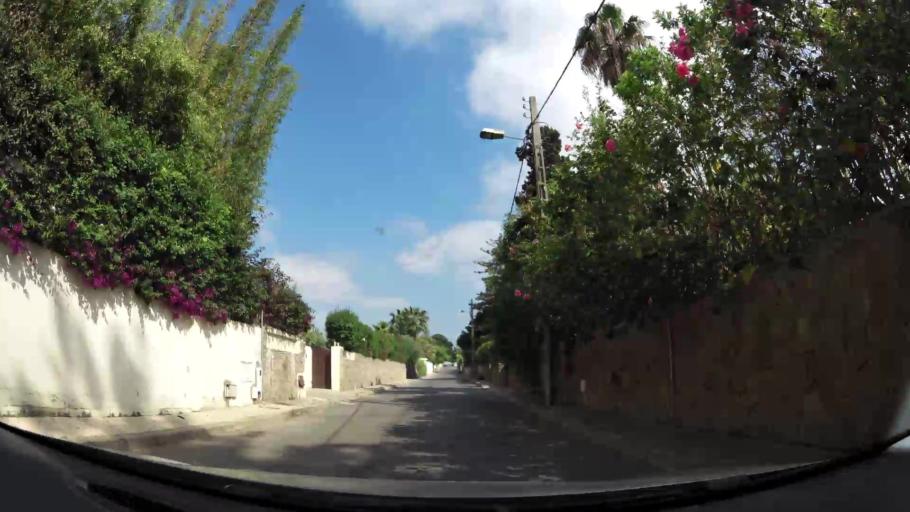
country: MA
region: Rabat-Sale-Zemmour-Zaer
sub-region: Rabat
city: Rabat
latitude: 33.9777
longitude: -6.8439
